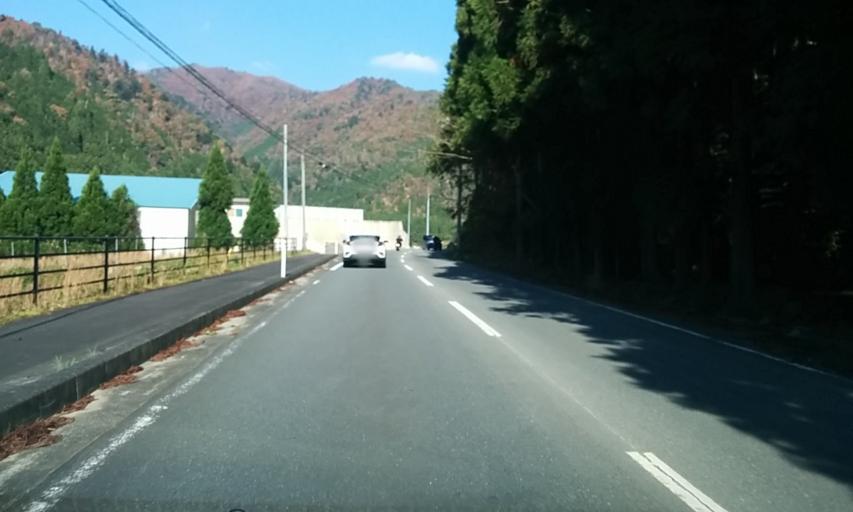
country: JP
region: Fukui
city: Obama
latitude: 35.2929
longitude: 135.6010
